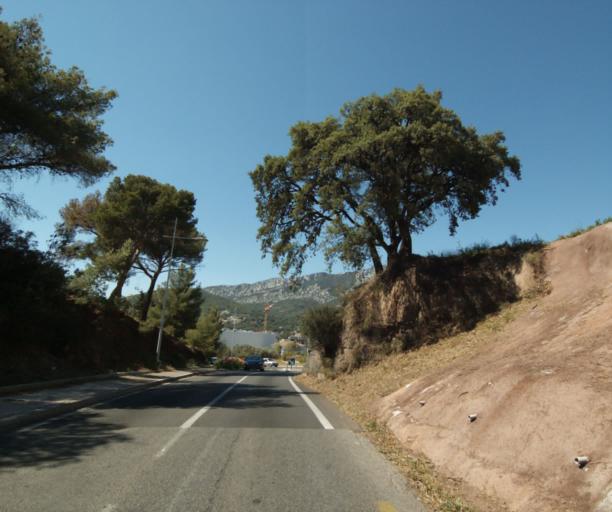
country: FR
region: Provence-Alpes-Cote d'Azur
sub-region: Departement du Var
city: La Garde
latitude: 43.1343
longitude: 6.0092
